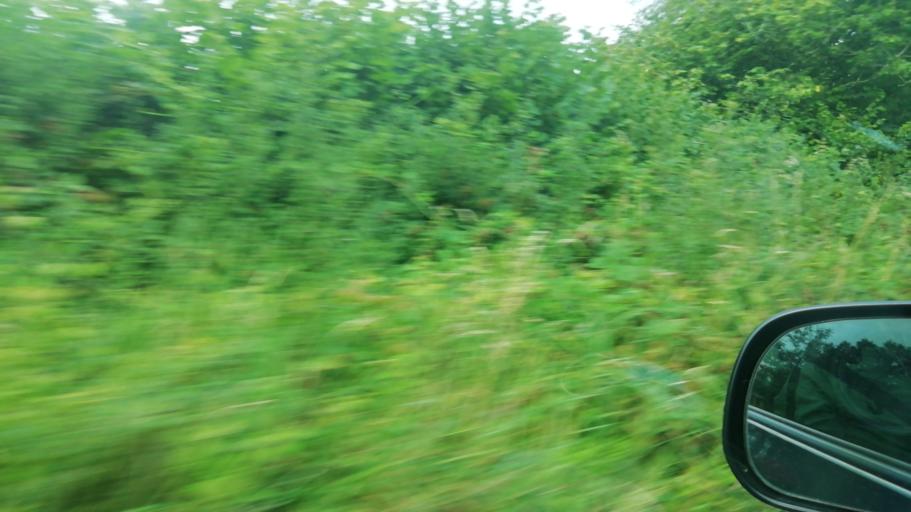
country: IE
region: Munster
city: Fethard
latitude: 52.5845
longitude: -7.5911
